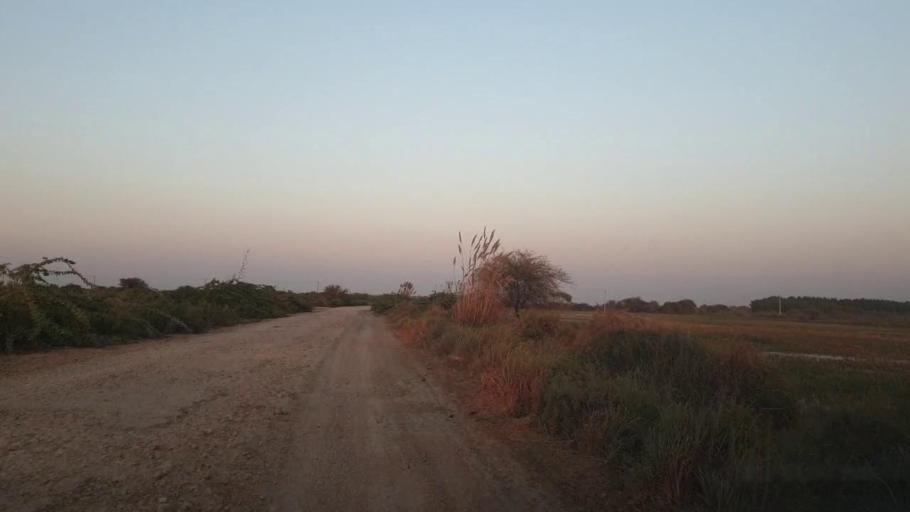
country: PK
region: Sindh
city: Mirpur Sakro
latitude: 24.4244
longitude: 67.5955
